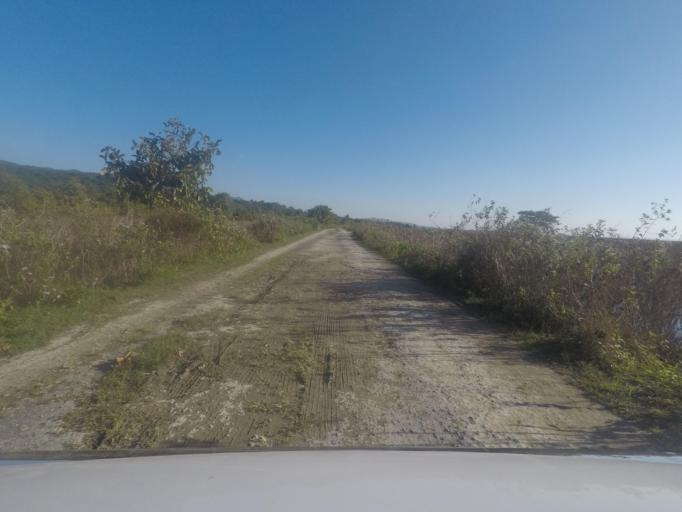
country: TL
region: Lautem
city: Lospalos
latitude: -8.4188
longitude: 127.1957
